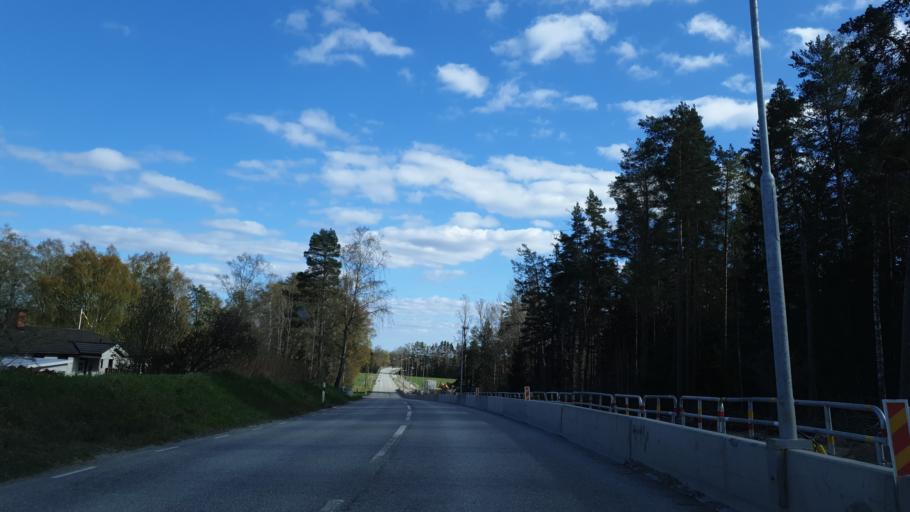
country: SE
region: Stockholm
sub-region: Sigtuna Kommun
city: Rosersberg
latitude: 59.5982
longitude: 17.8833
